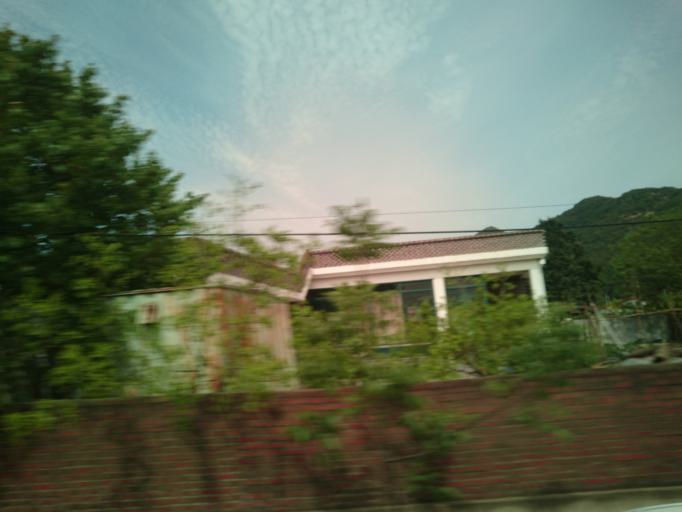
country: KR
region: Jeollabuk-do
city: Wanju
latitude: 35.8969
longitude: 127.1914
